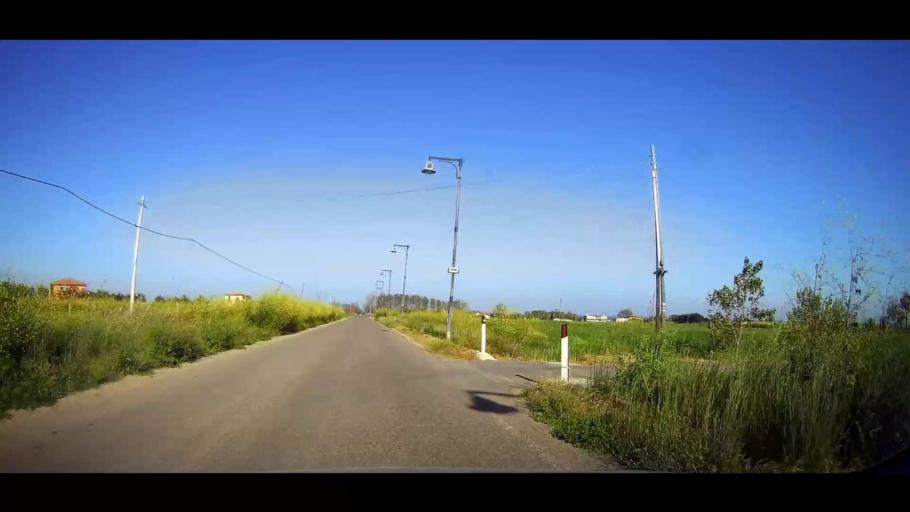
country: IT
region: Calabria
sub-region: Provincia di Crotone
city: Crotone
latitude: 39.0251
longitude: 17.1814
